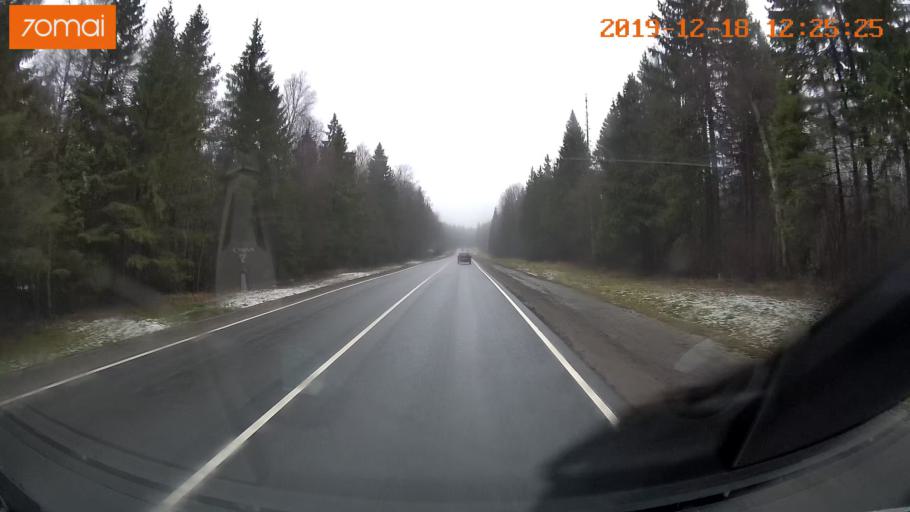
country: RU
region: Moskovskaya
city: Novopetrovskoye
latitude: 56.0377
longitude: 36.4995
